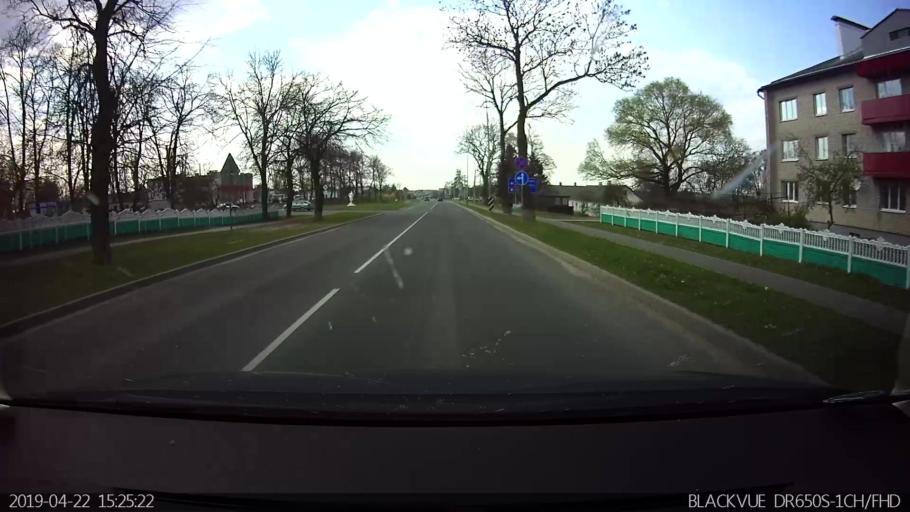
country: BY
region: Brest
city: Vysokaye
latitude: 52.3643
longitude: 23.3964
